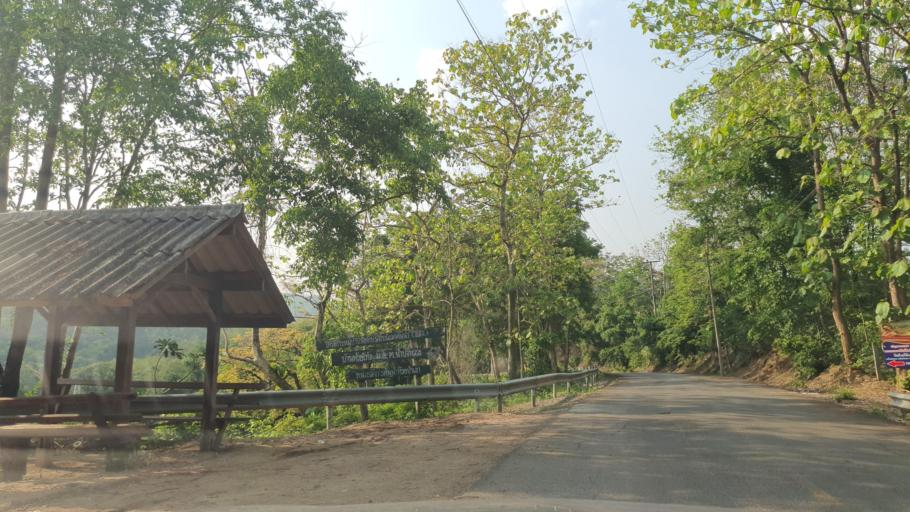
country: TH
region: Chiang Mai
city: Mae Wang
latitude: 18.6924
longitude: 98.8132
